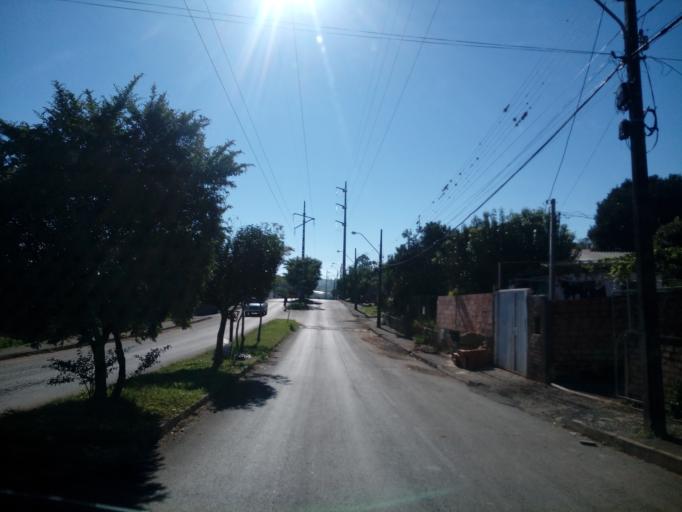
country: BR
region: Santa Catarina
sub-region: Chapeco
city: Chapeco
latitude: -27.0665
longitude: -52.6045
